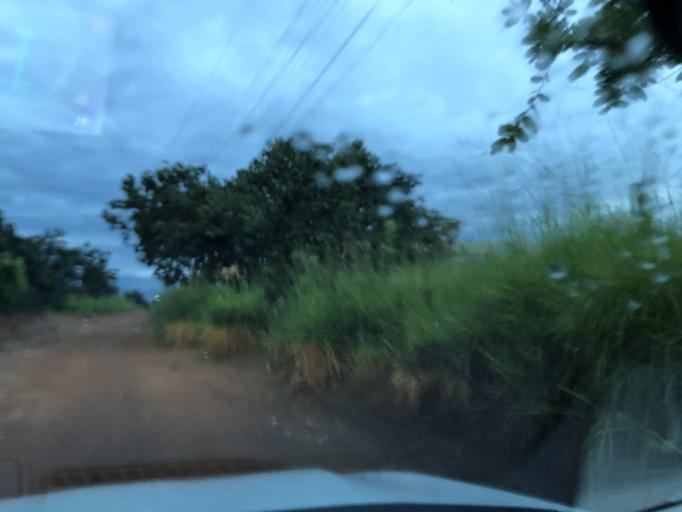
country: BR
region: Goias
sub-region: Luziania
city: Luziania
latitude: -16.1172
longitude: -47.9878
